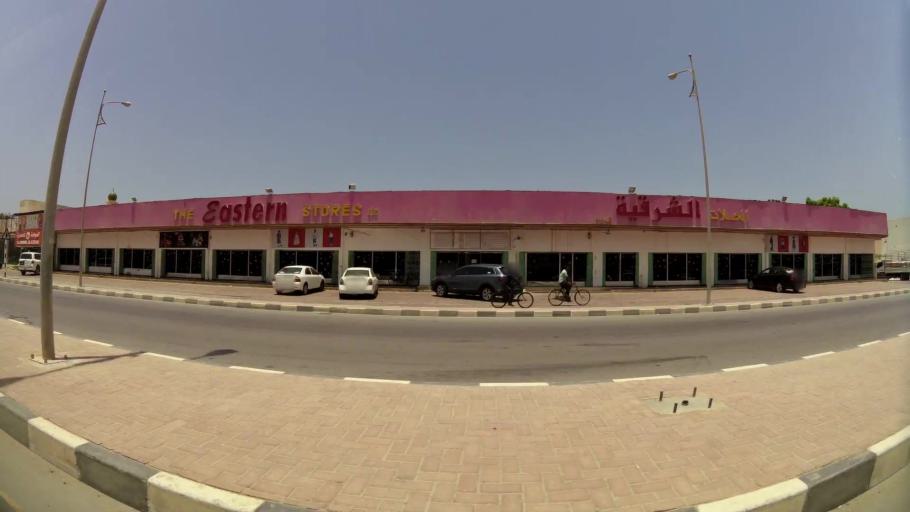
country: OM
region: Zufar
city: Salalah
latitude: 17.0195
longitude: 54.1119
